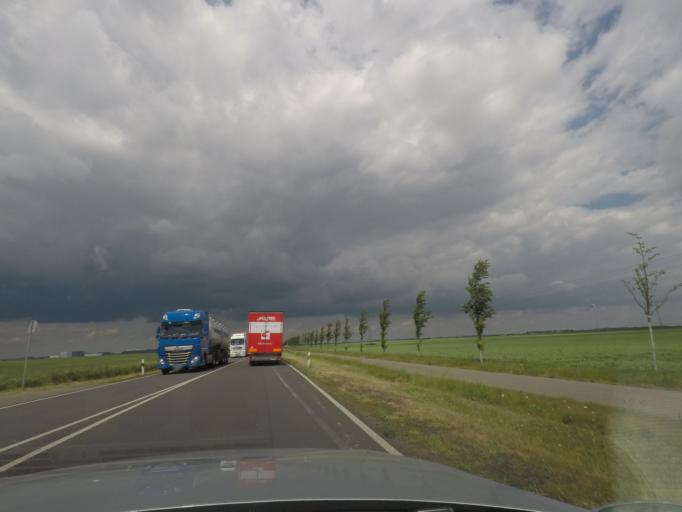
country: DE
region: Saxony
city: Markranstadt
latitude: 51.3168
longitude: 12.2114
